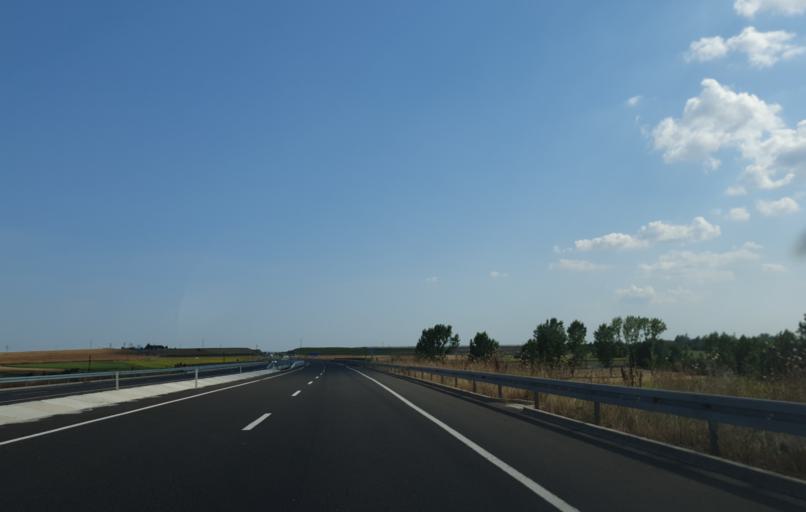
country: TR
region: Tekirdag
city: Muratli
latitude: 41.2198
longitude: 27.5323
